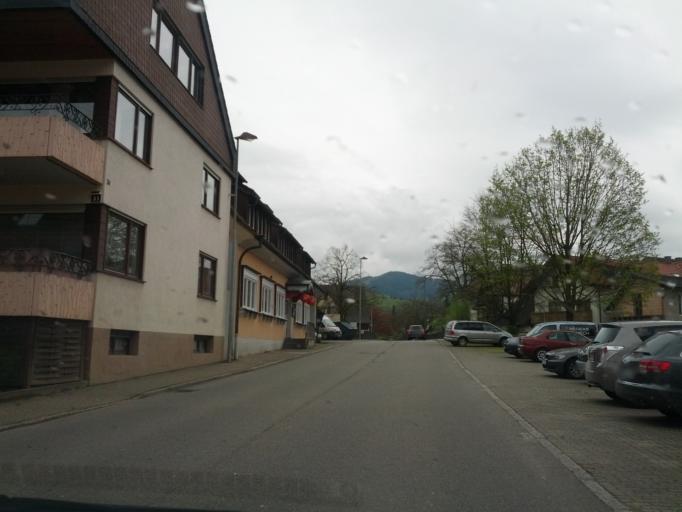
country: DE
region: Baden-Wuerttemberg
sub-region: Freiburg Region
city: Pfaffenweiler
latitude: 47.9144
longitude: 7.7545
